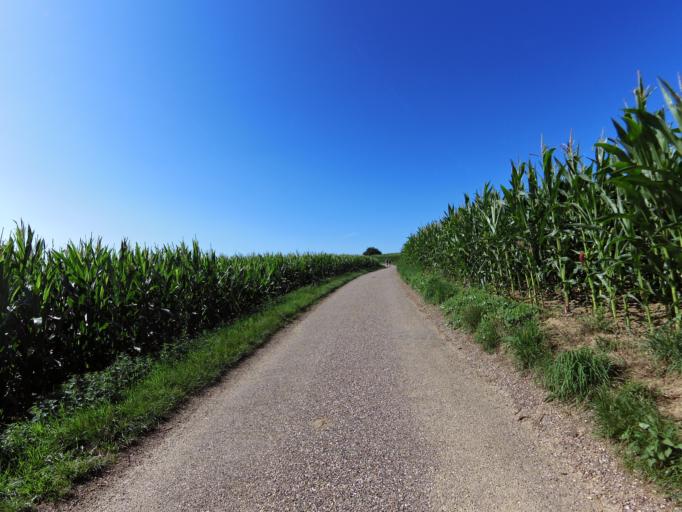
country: NL
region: Limburg
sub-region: Gemeente Voerendaal
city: Ubachsberg
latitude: 50.8195
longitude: 5.9446
